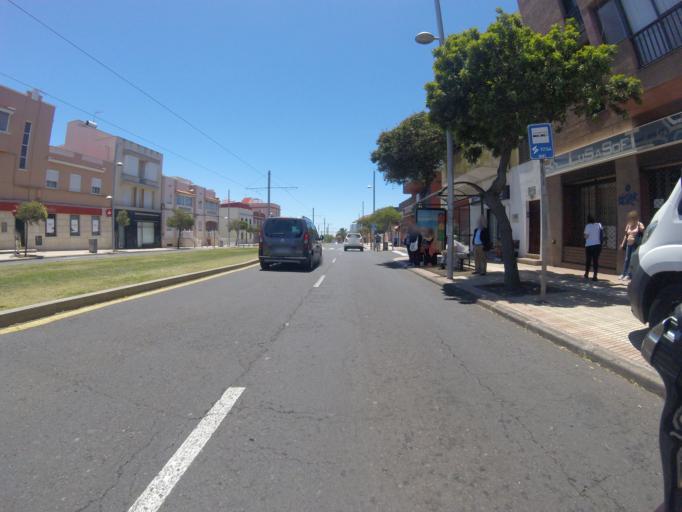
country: ES
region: Canary Islands
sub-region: Provincia de Santa Cruz de Tenerife
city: La Laguna
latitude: 28.4787
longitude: -16.3117
